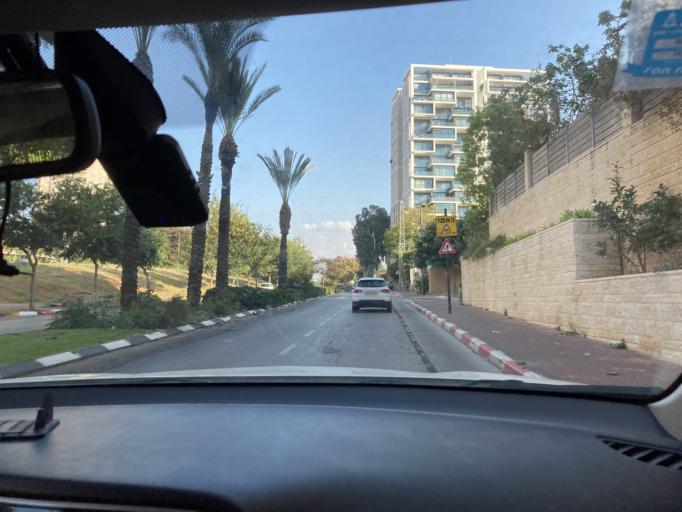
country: IL
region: Tel Aviv
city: Ramat HaSharon
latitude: 32.1507
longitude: 34.8440
